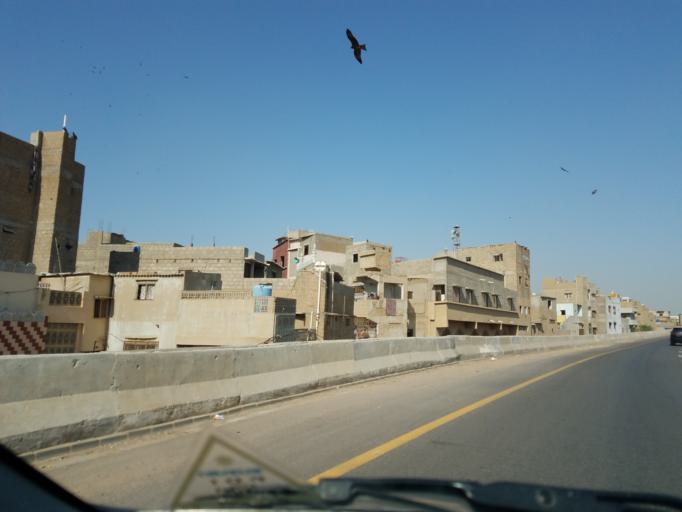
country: PK
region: Sindh
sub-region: Karachi District
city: Karachi
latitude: 24.8896
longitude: 67.0266
